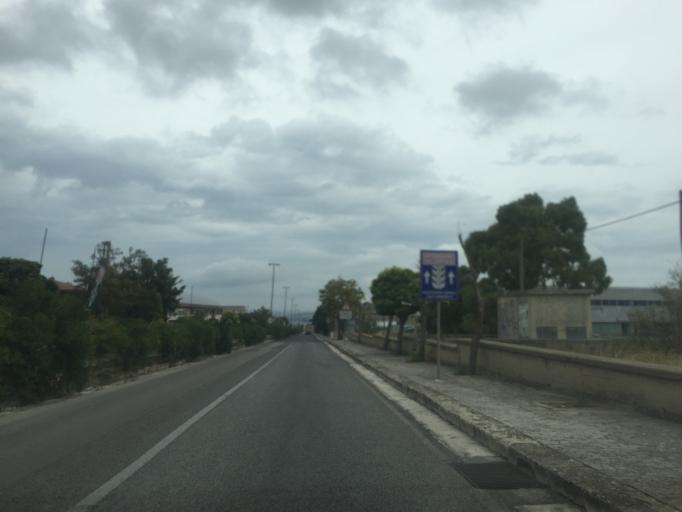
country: IT
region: Sicily
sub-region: Ragusa
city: Ragusa
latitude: 36.9024
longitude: 14.7160
